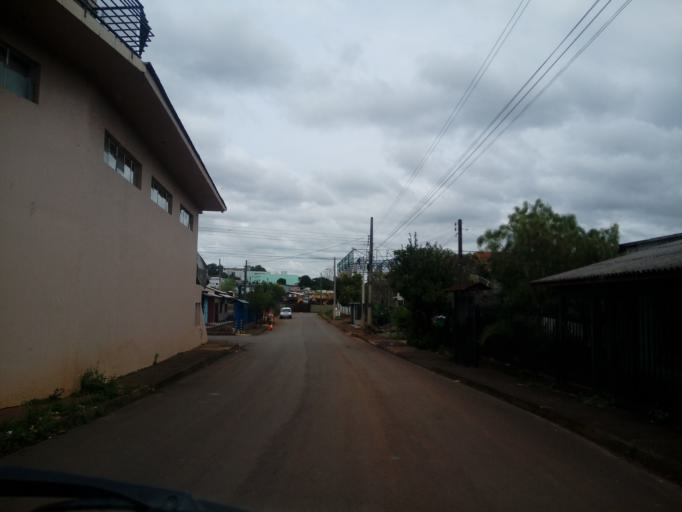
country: BR
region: Santa Catarina
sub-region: Chapeco
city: Chapeco
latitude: -27.0703
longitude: -52.6201
